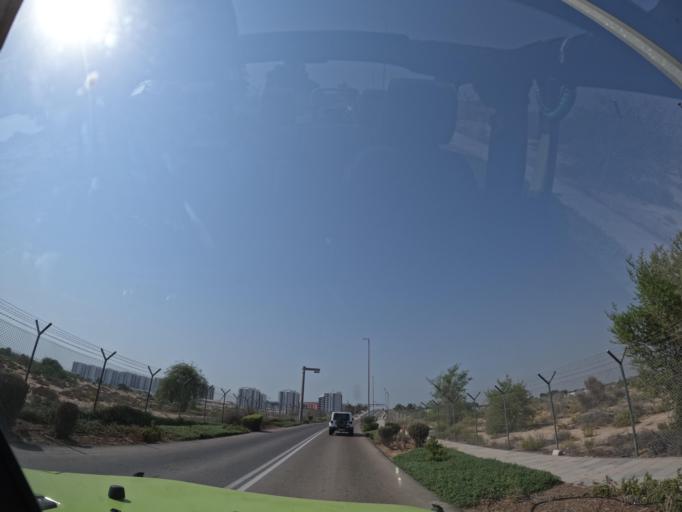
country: AE
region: Abu Dhabi
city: Abu Dhabi
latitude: 24.4784
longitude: 54.6256
